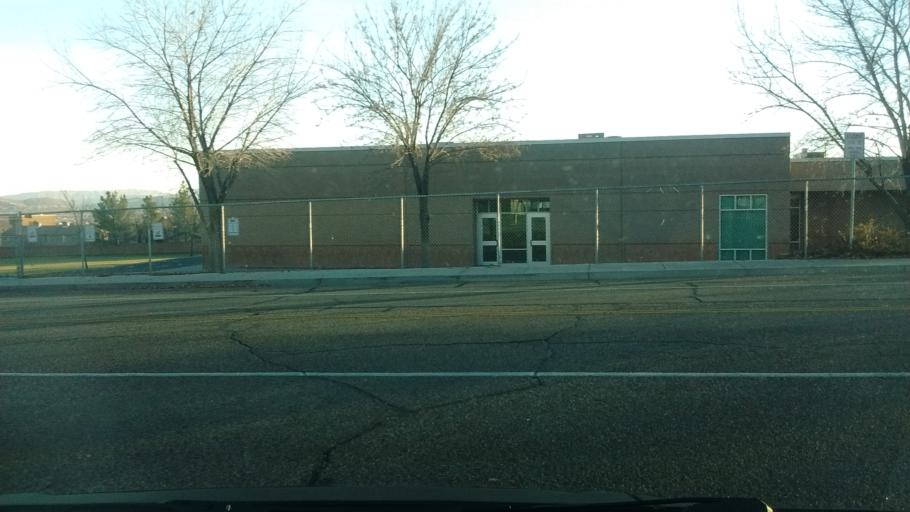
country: US
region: Utah
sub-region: Washington County
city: Washington
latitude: 37.1230
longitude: -113.5302
